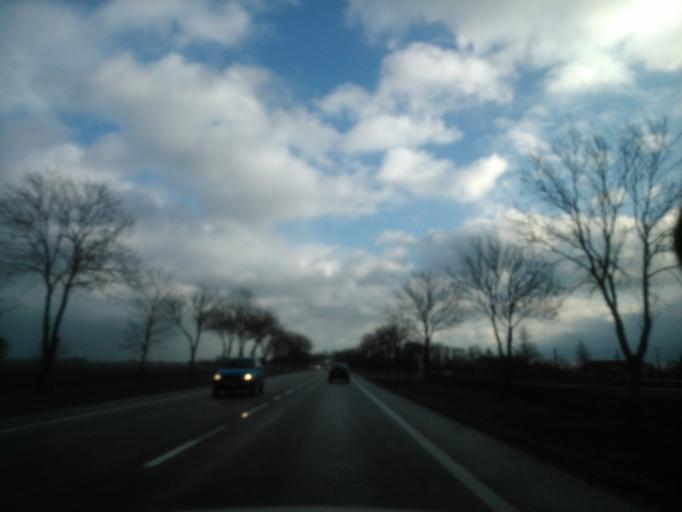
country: PL
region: Masovian Voivodeship
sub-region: Powiat sierpecki
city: Rosciszewo
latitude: 52.8273
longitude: 19.7600
